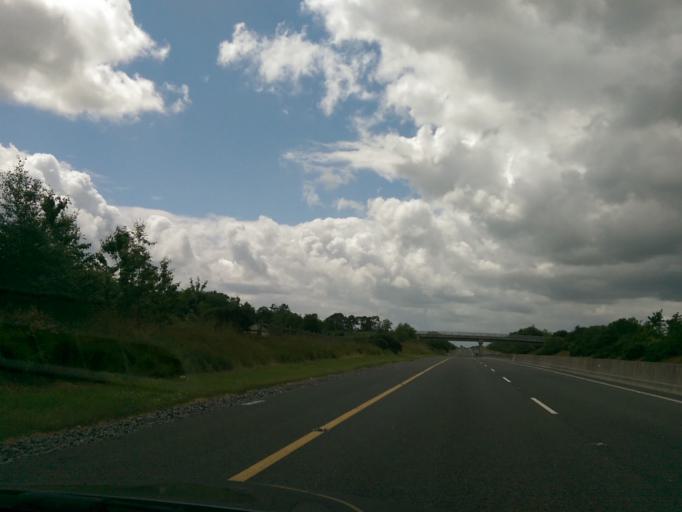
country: IE
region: Munster
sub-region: County Cork
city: Mitchelstown
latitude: 52.3098
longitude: -8.1498
